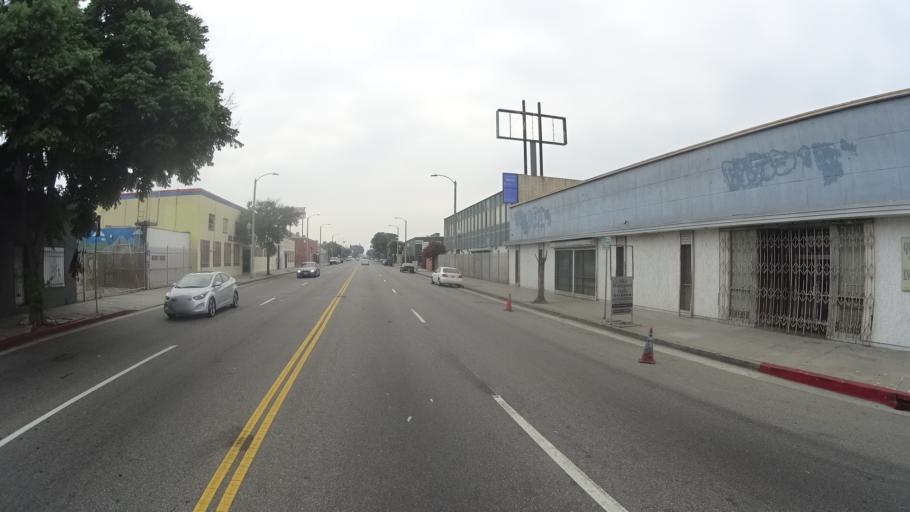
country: US
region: California
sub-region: Los Angeles County
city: View Park-Windsor Hills
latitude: 34.0256
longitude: -118.3337
